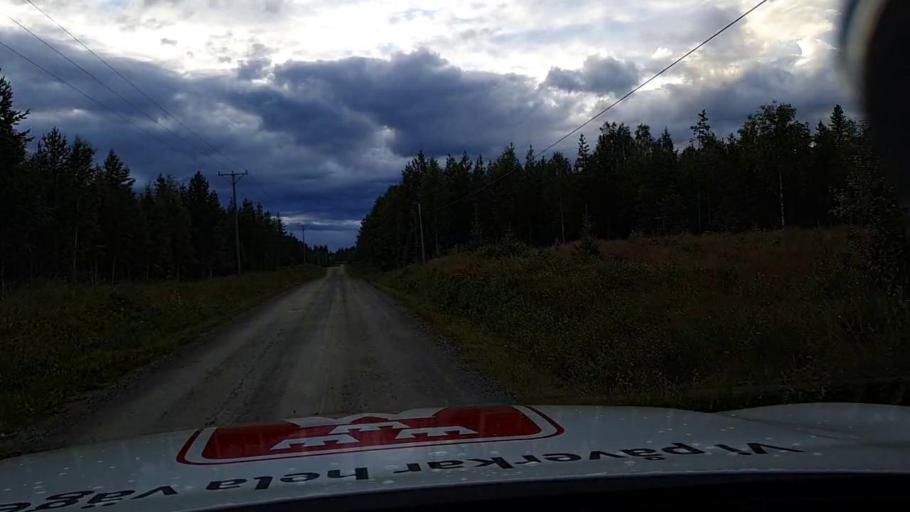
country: SE
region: Jaemtland
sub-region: Bergs Kommun
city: Hoverberg
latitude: 62.8893
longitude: 14.5693
